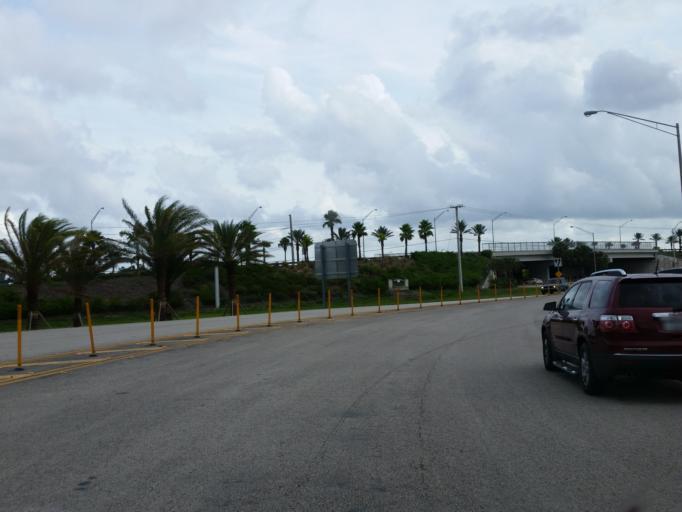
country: US
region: Florida
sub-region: Saint Lucie County
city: Port Saint Lucie
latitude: 27.2748
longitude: -80.3571
